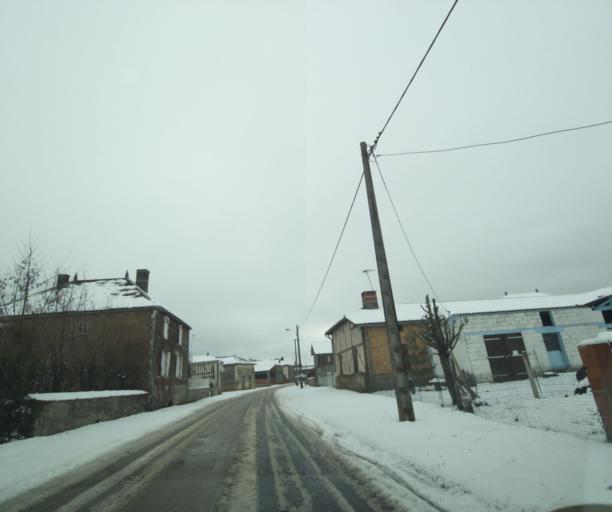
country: FR
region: Champagne-Ardenne
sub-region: Departement de la Haute-Marne
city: Montier-en-Der
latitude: 48.4329
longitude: 4.7272
